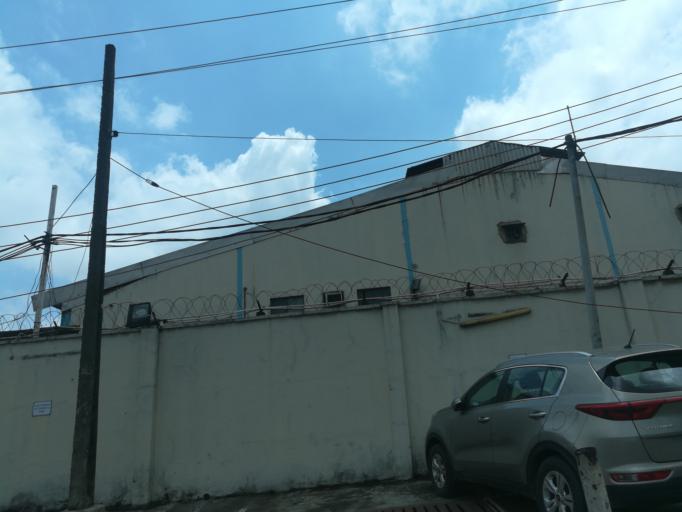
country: NG
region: Lagos
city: Oshodi
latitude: 6.5545
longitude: 3.3583
